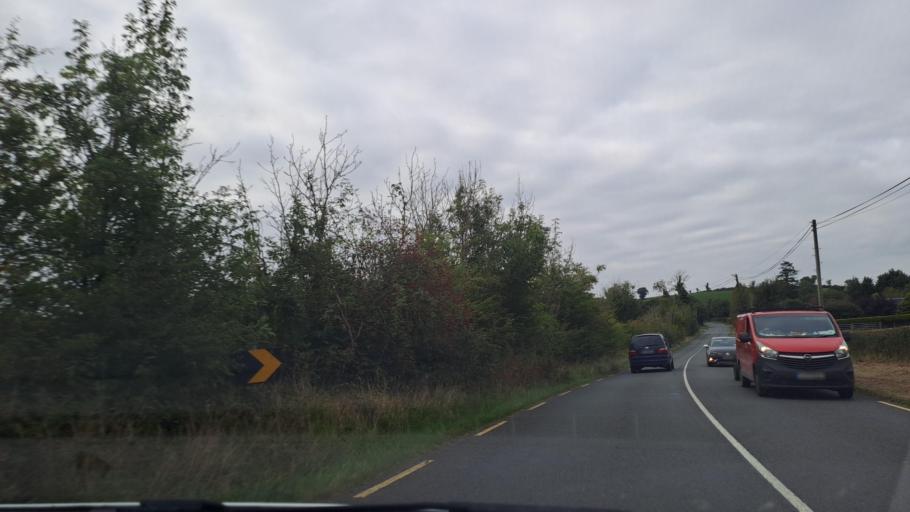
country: IE
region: Ulster
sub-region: County Monaghan
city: Carrickmacross
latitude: 53.9977
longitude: -6.7337
